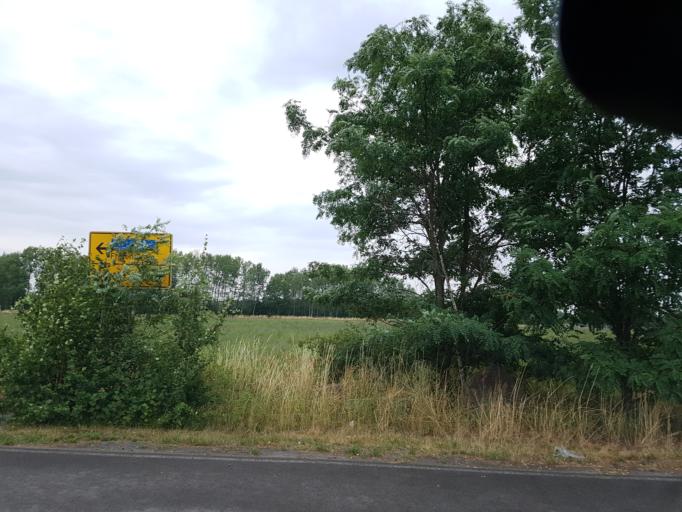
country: DE
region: Brandenburg
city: Schipkau
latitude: 51.5441
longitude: 13.9290
